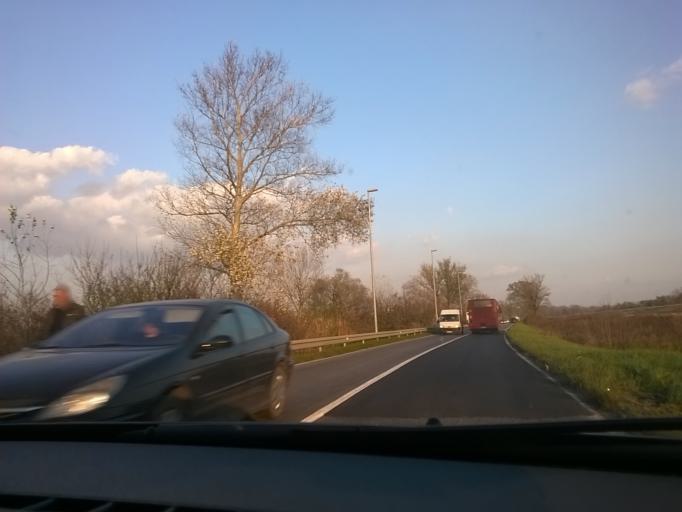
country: RS
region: Autonomna Pokrajina Vojvodina
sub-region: Juznobanatski Okrug
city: Pancevo
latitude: 44.8696
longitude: 20.6031
